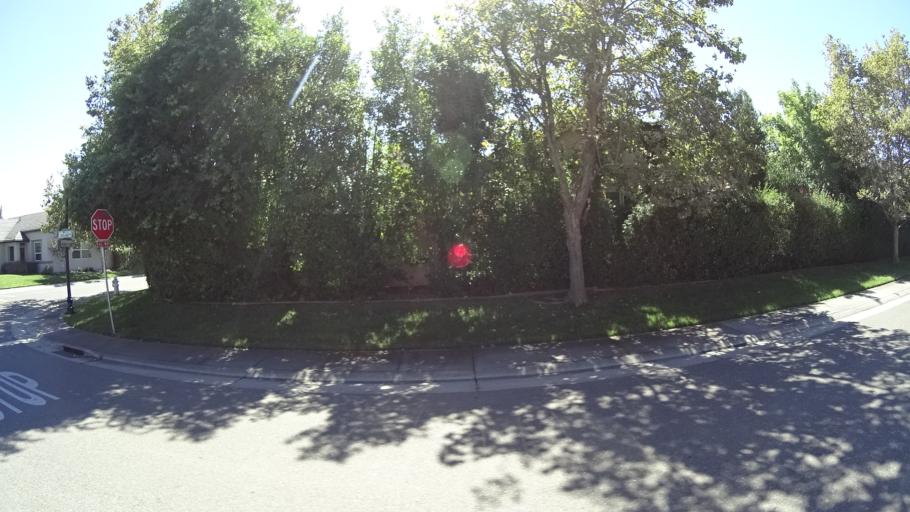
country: US
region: California
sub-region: Sacramento County
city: Laguna
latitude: 38.4132
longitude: -121.4623
